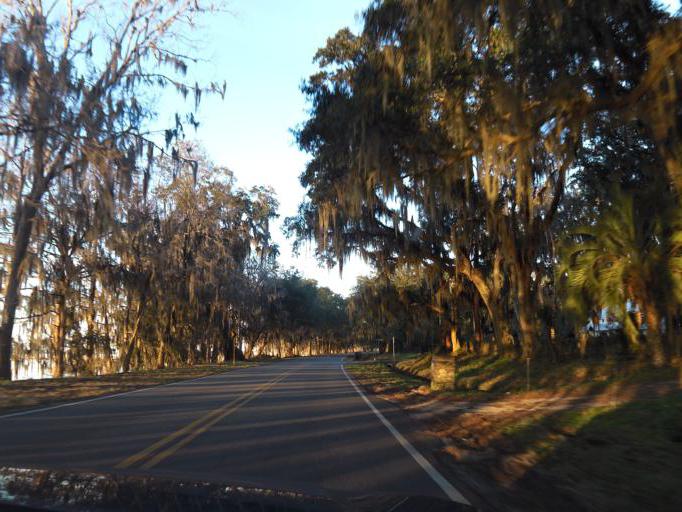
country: US
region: Florida
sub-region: Clay County
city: Green Cove Springs
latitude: 29.9203
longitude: -81.5945
